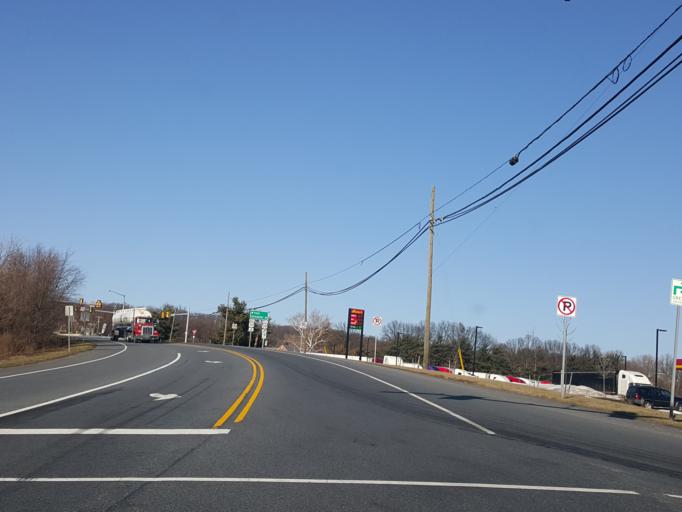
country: US
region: Pennsylvania
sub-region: Lancaster County
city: Mountville
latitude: 40.0436
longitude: -76.4229
